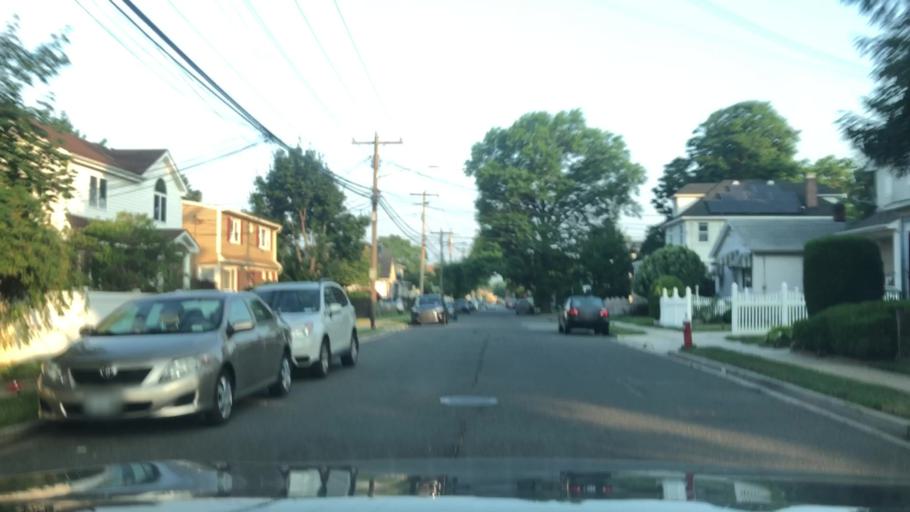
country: US
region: New York
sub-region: Nassau County
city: Elmont
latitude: 40.7051
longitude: -73.7044
